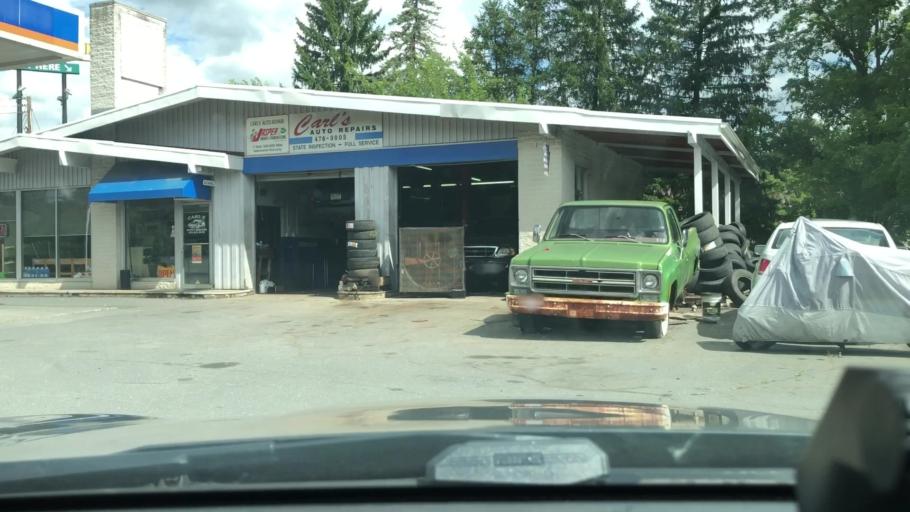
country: US
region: Pennsylvania
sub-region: Monroe County
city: Arlington Heights
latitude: 40.9825
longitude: -75.2120
